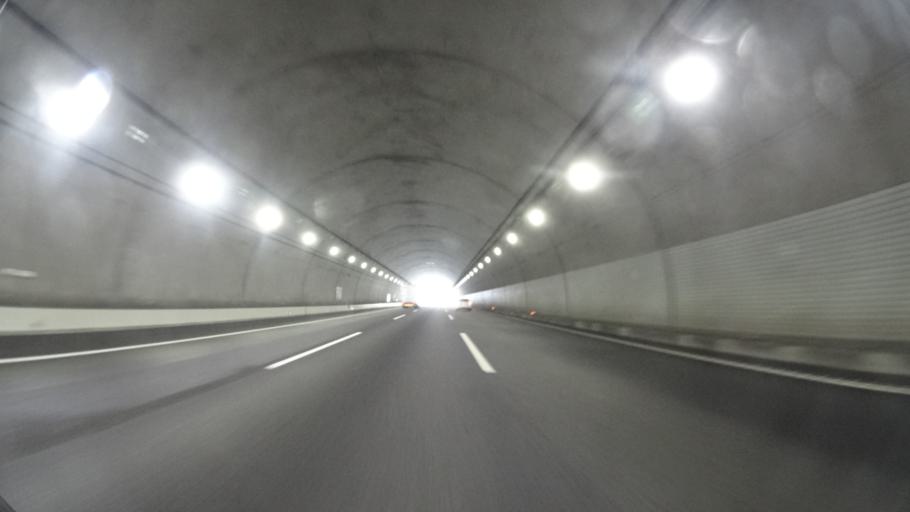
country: JP
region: Shizuoka
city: Fujinomiya
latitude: 35.1932
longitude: 138.6327
